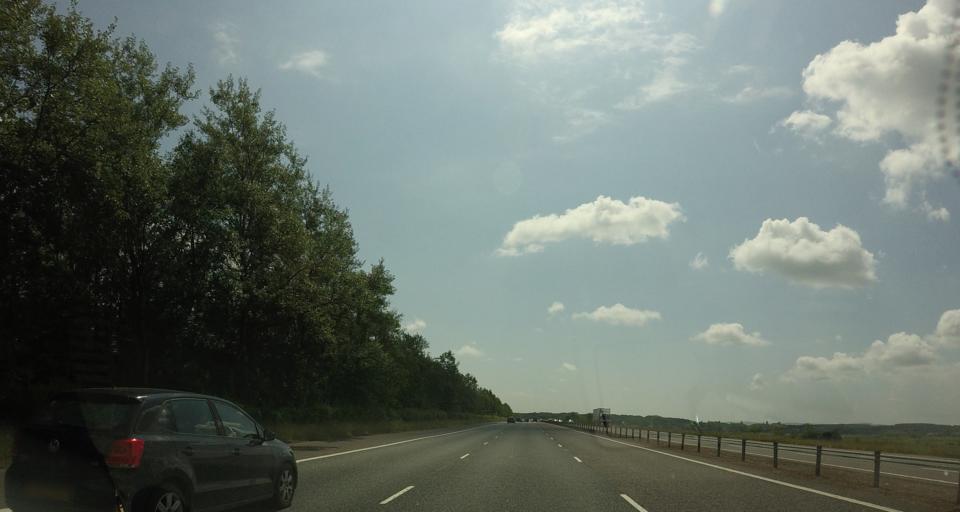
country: GB
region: Scotland
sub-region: Dumfries and Galloway
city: Lochmaben
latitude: 55.1933
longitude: -3.4090
